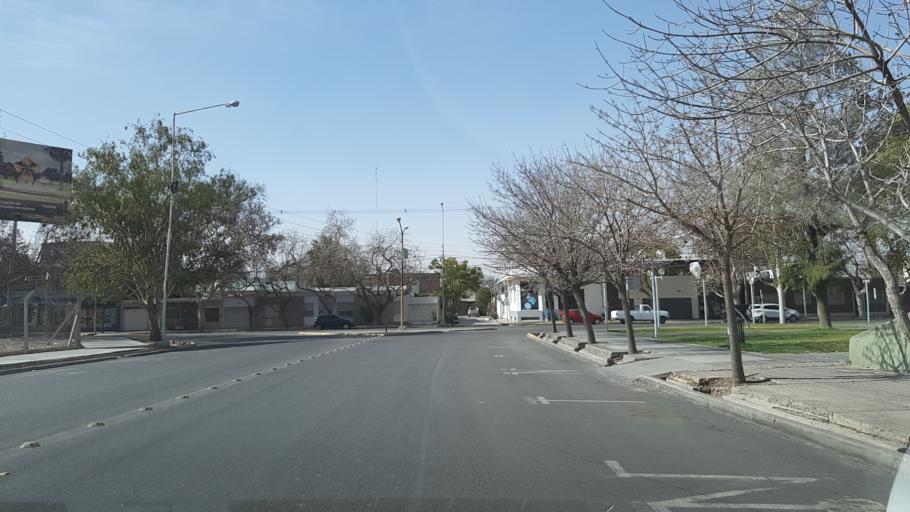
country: AR
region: San Juan
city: San Juan
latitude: -31.5320
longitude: -68.5378
